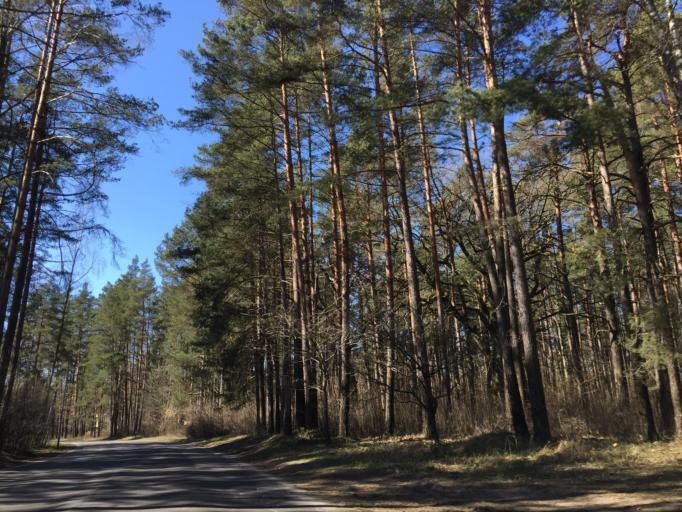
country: LV
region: Jurmala
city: Jurmala
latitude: 56.9484
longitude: 23.7458
